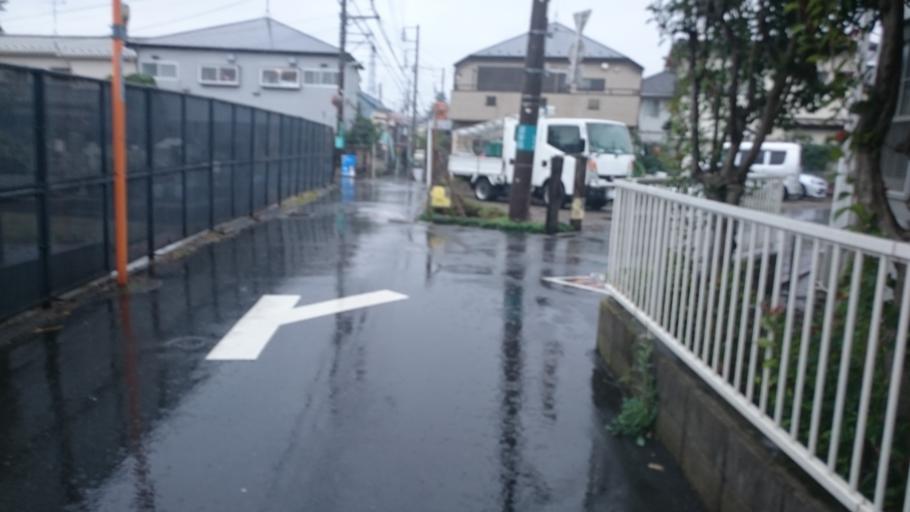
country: JP
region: Tokyo
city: Kokubunji
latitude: 35.6833
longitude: 139.4904
